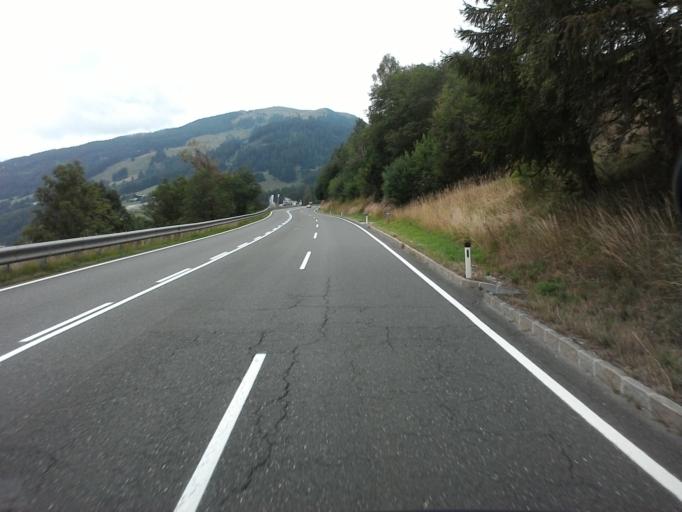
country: AT
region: Salzburg
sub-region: Politischer Bezirk Zell am See
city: Hollersbach im Pinzgau
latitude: 47.2971
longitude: 12.4248
